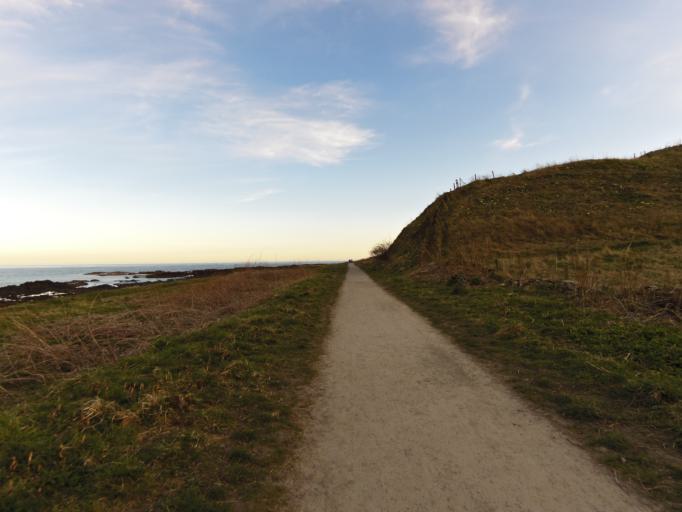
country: GB
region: Scotland
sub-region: Aberdeenshire
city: Inverbervie
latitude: 56.8371
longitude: -2.2756
